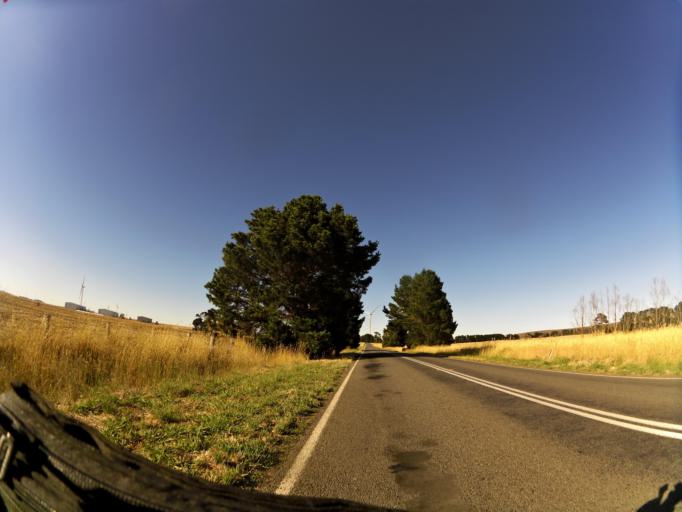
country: AU
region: Victoria
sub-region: Ballarat North
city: Delacombe
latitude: -37.5595
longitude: 143.3630
